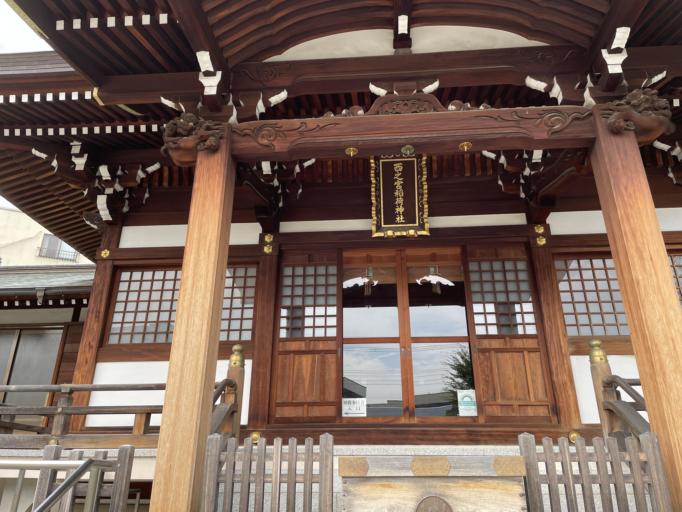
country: JP
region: Saitama
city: Soka
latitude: 35.7640
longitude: 139.8115
